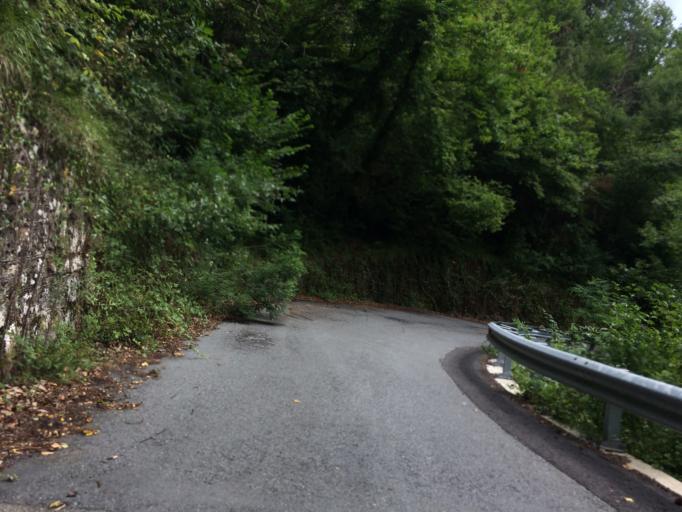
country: IT
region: Liguria
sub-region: Provincia di Imperia
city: Castel Vittorio
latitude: 43.9395
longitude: 7.6847
